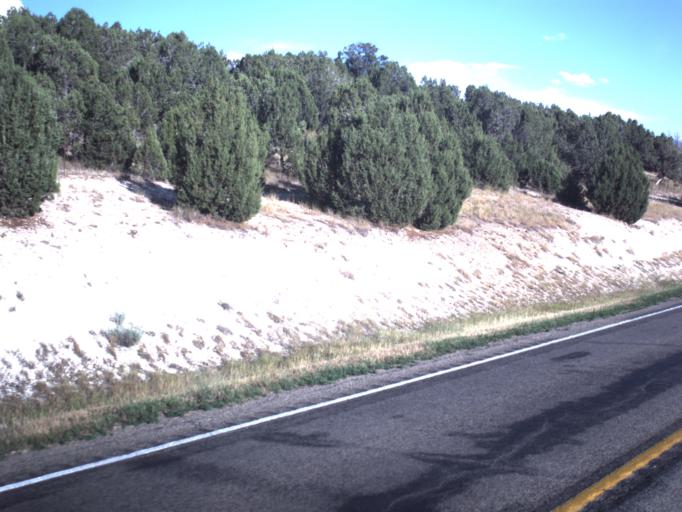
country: US
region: Utah
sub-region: Sanpete County
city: Fairview
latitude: 39.6481
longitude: -111.4510
